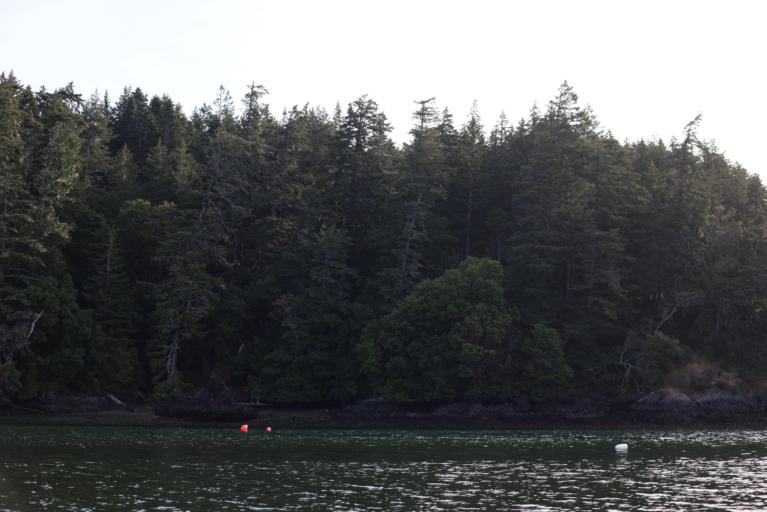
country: CA
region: British Columbia
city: Metchosin
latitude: 48.3421
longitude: -123.5570
